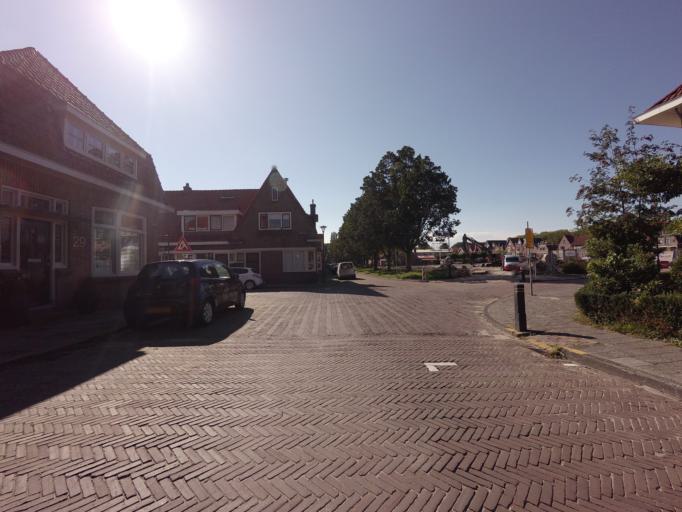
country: NL
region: North Holland
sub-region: Gemeente Enkhuizen
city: Enkhuizen
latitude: 52.7002
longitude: 5.2840
